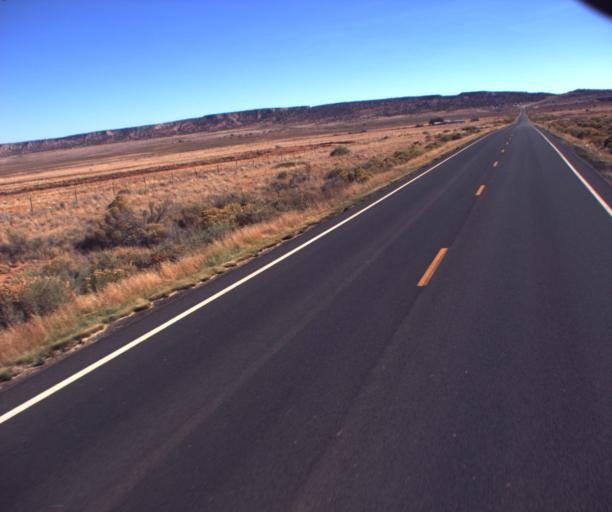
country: US
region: Arizona
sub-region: Apache County
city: Ganado
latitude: 35.7706
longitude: -109.6473
